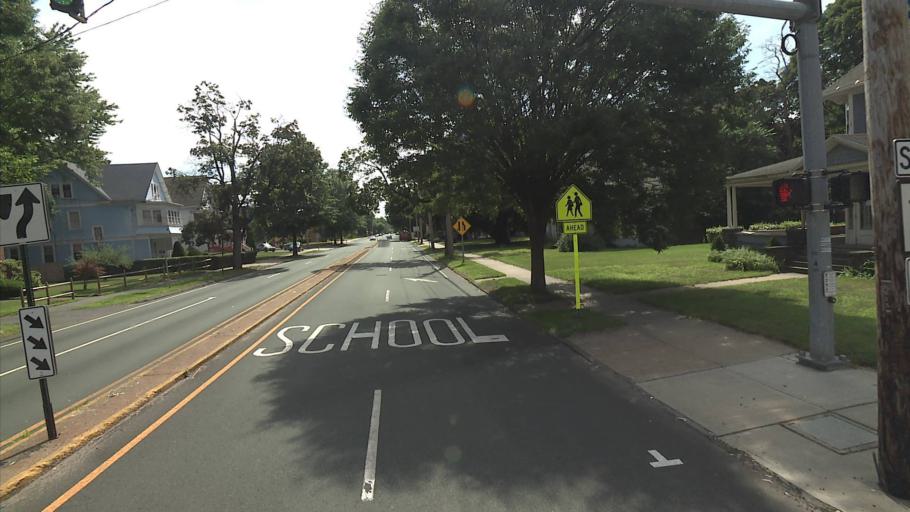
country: US
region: Connecticut
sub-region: New Haven County
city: New Haven
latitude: 41.3272
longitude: -72.9681
